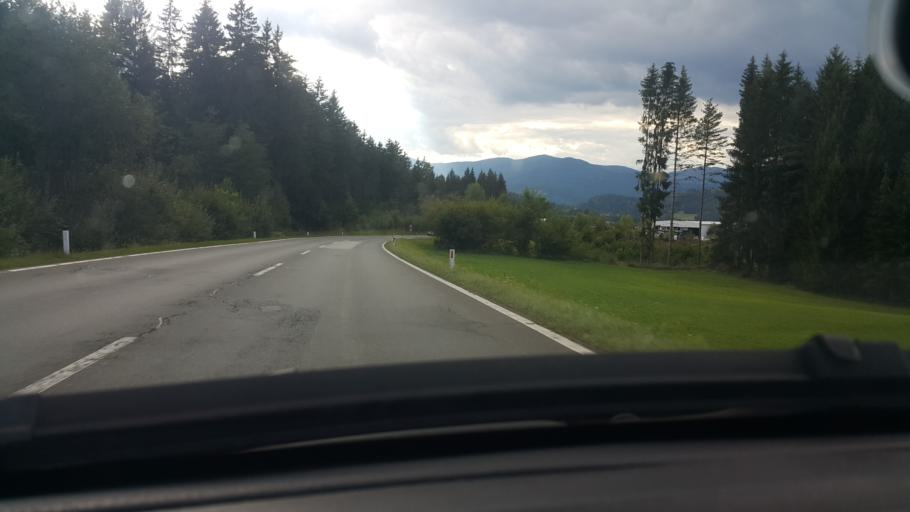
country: AT
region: Carinthia
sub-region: Politischer Bezirk Feldkirchen
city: Feldkirchen in Karnten
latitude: 46.6921
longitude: 14.1319
